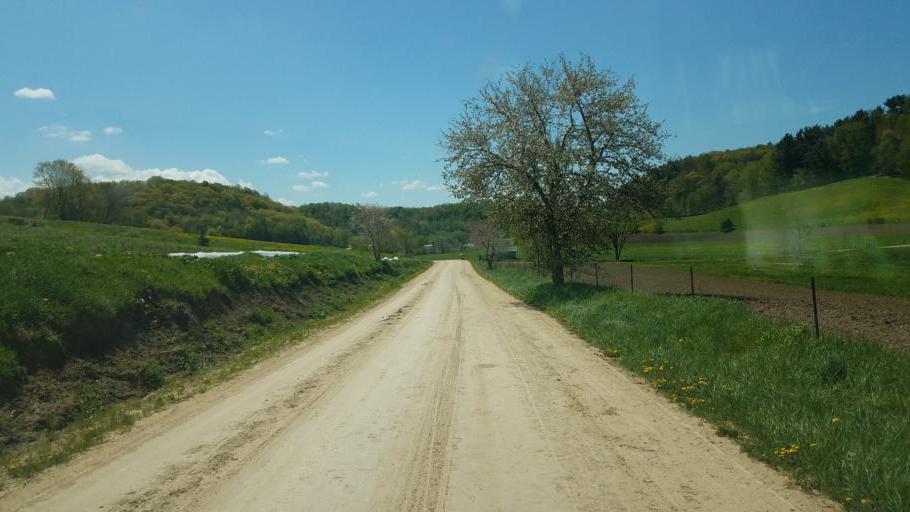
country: US
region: Wisconsin
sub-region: Vernon County
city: Hillsboro
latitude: 43.5877
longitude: -90.4077
